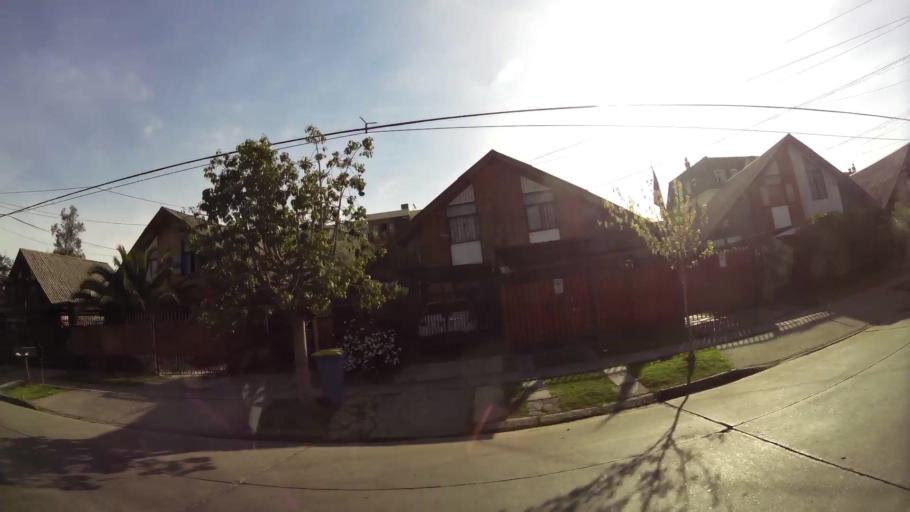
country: CL
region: Santiago Metropolitan
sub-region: Provincia de Santiago
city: Villa Presidente Frei, Nunoa, Santiago, Chile
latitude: -33.5234
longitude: -70.5826
